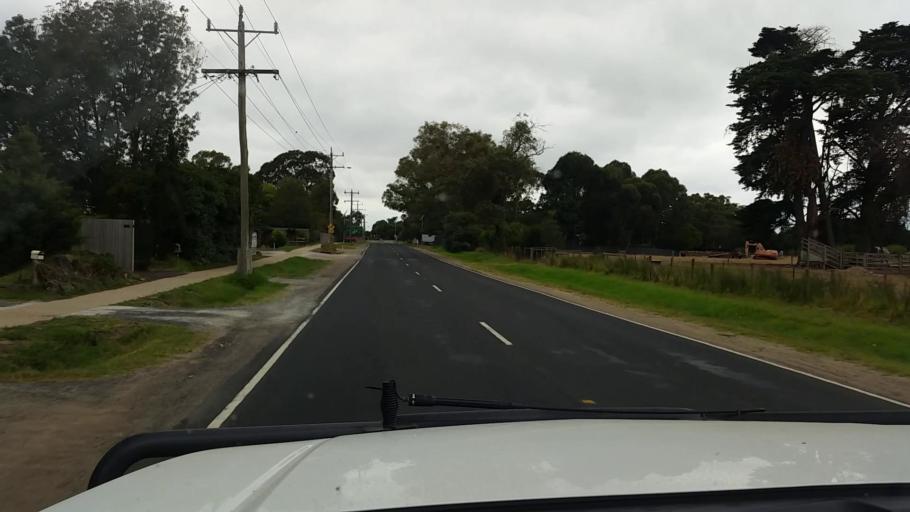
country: AU
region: Victoria
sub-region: Mornington Peninsula
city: Langwarrin South
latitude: -38.1985
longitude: 145.1779
